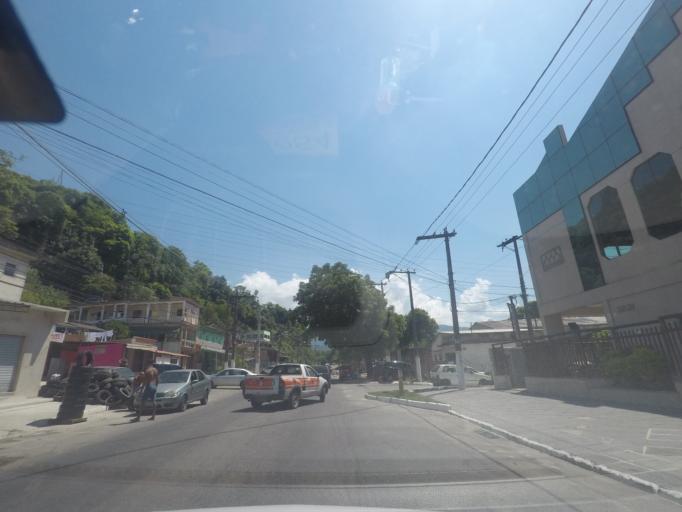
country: BR
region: Rio de Janeiro
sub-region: Petropolis
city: Petropolis
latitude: -22.6015
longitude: -43.1889
